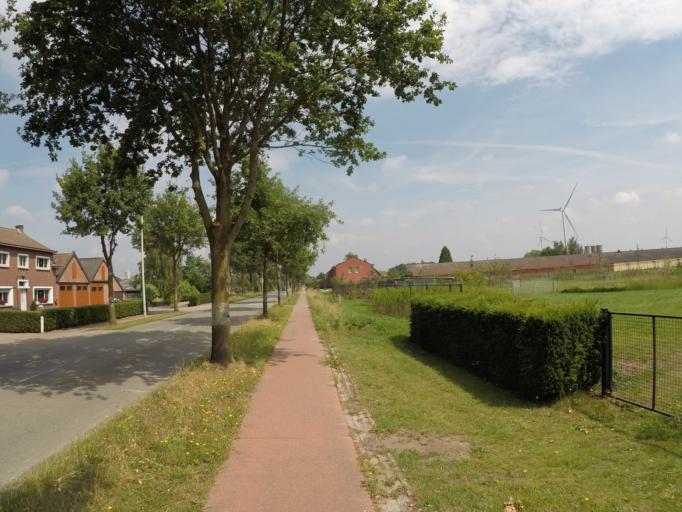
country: BE
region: Flanders
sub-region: Provincie Antwerpen
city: Brecht
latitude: 51.3711
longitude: 4.6441
